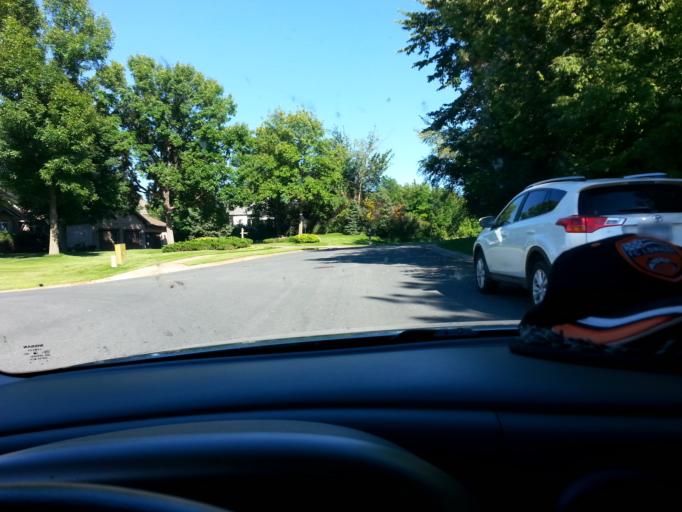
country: US
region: Minnesota
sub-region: Scott County
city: Prior Lake
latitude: 44.7277
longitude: -93.4471
